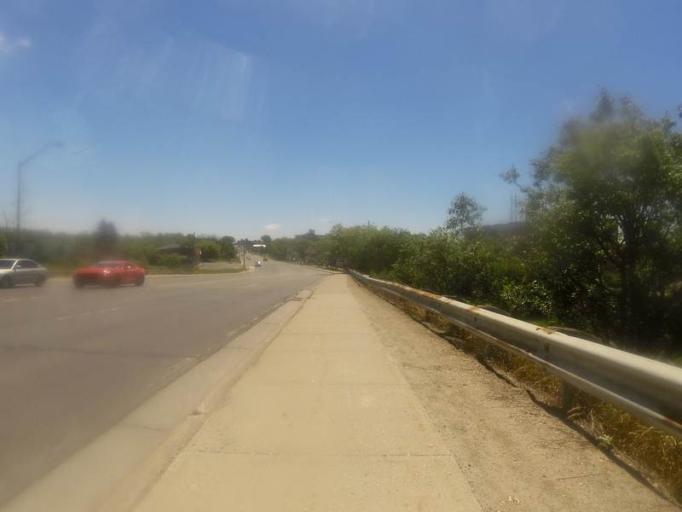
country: CA
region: Ontario
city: Kingston
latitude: 44.2539
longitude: -76.5380
